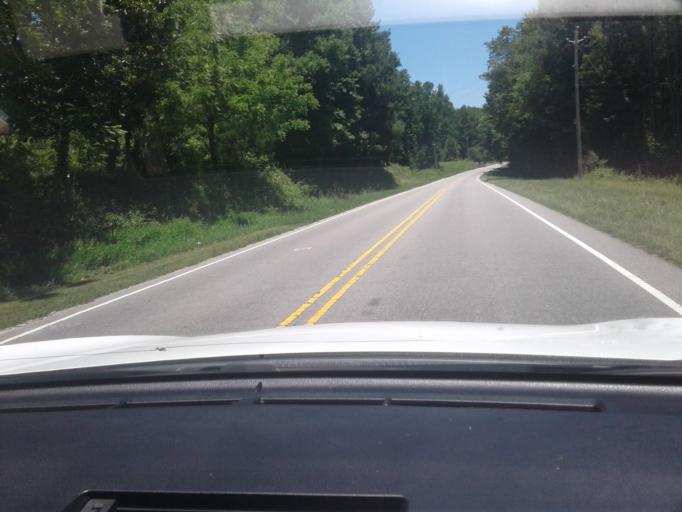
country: US
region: North Carolina
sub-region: Harnett County
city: Lillington
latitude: 35.3744
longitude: -78.8514
